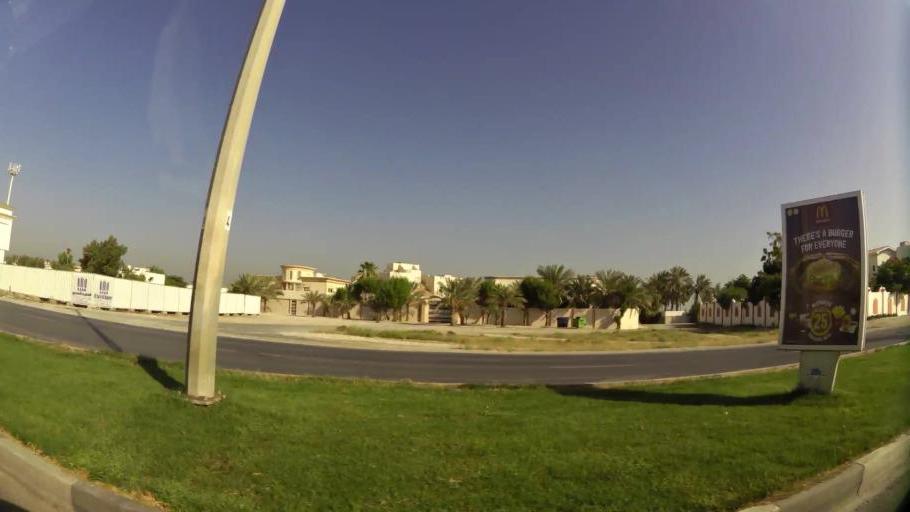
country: AE
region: Ajman
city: Ajman
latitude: 25.3829
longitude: 55.4076
